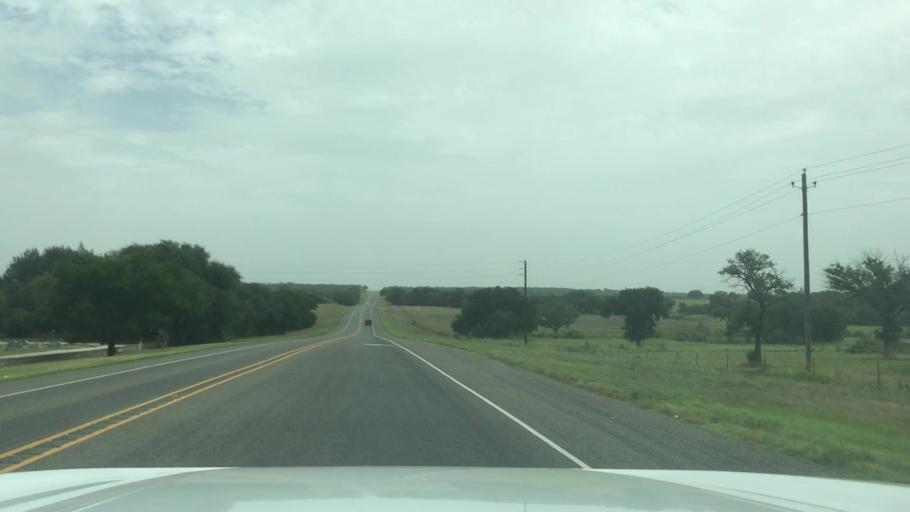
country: US
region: Texas
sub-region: Hamilton County
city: Hico
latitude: 31.9810
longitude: -98.0139
